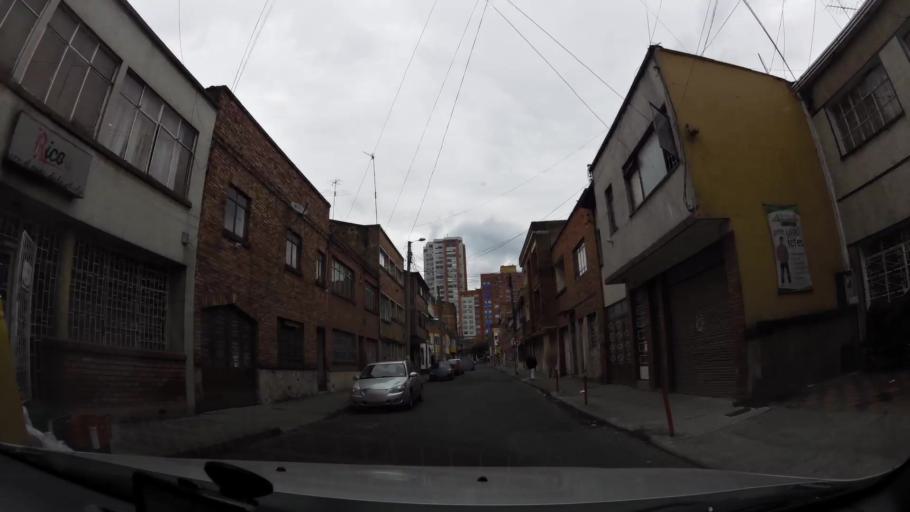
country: CO
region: Bogota D.C.
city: Bogota
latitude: 4.6314
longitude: -74.0846
